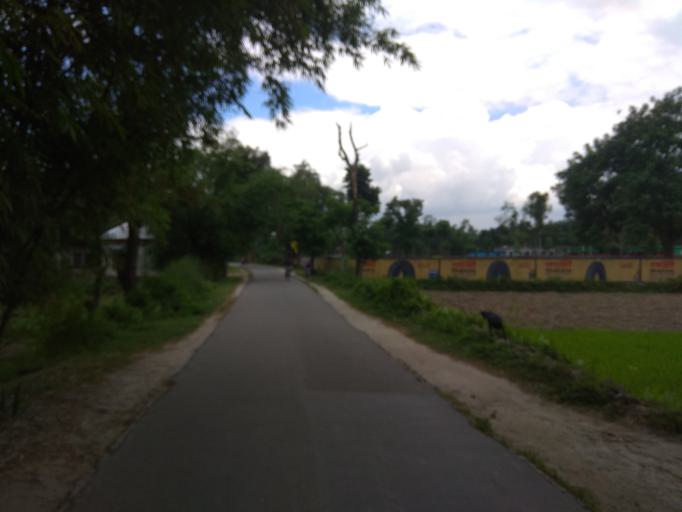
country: IN
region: West Bengal
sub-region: Koch Bihar
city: Haldibari
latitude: 26.1961
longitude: 88.9229
